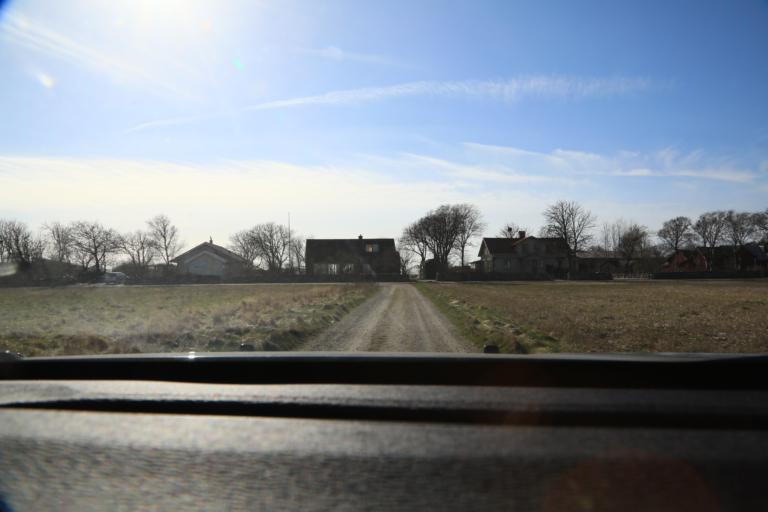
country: SE
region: Halland
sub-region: Varbergs Kommun
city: Varberg
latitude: 57.1230
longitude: 12.2129
